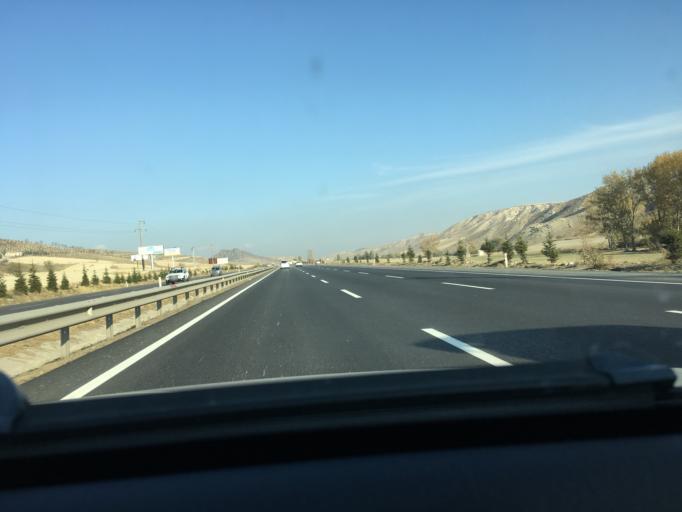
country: TR
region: Ankara
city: Temelli
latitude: 39.7613
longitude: 32.4653
